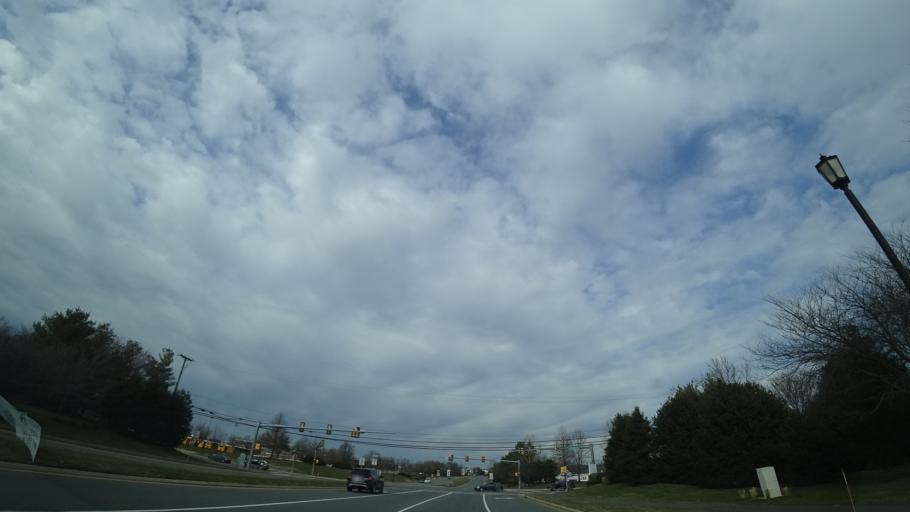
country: US
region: Virginia
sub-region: Loudoun County
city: Belmont
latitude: 39.0454
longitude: -77.5077
